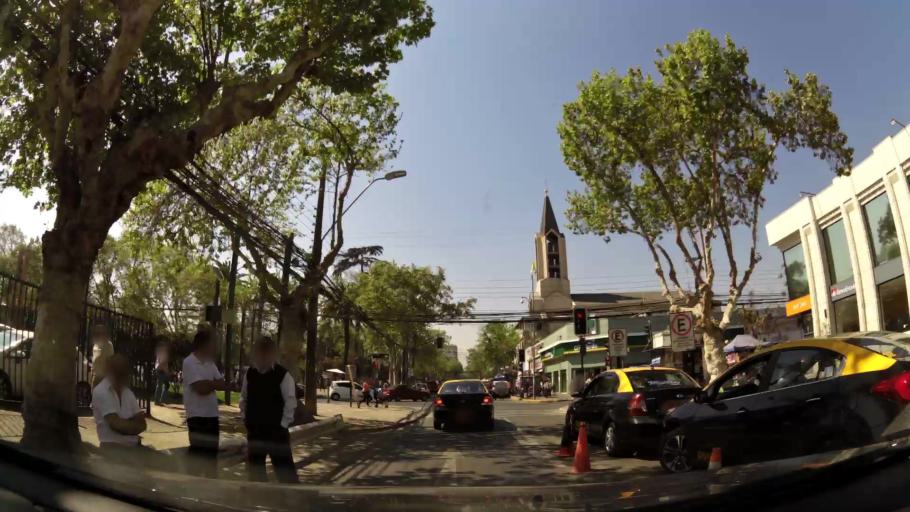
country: CL
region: Santiago Metropolitan
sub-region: Provincia de Maipo
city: San Bernardo
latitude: -33.5926
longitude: -70.7055
